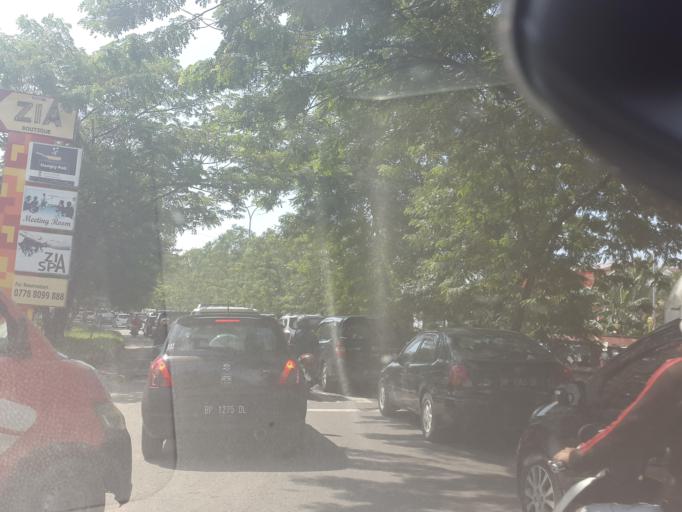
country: SG
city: Singapore
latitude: 1.1332
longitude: 104.0292
